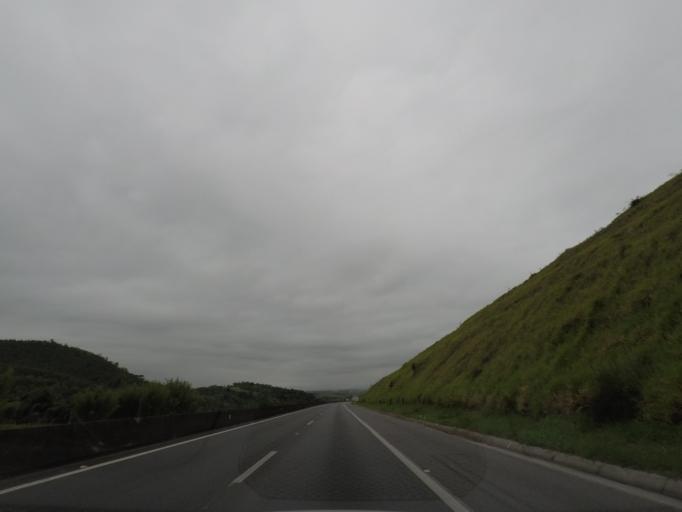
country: BR
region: Sao Paulo
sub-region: Jacarei
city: Jacarei
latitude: -23.2506
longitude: -46.0760
